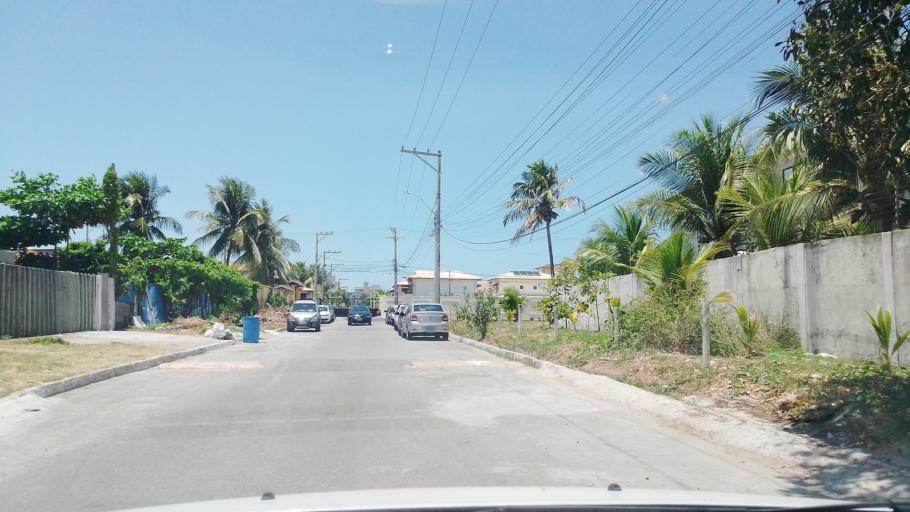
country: BR
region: Bahia
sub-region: Lauro De Freitas
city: Lauro de Freitas
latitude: -12.9383
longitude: -38.3307
